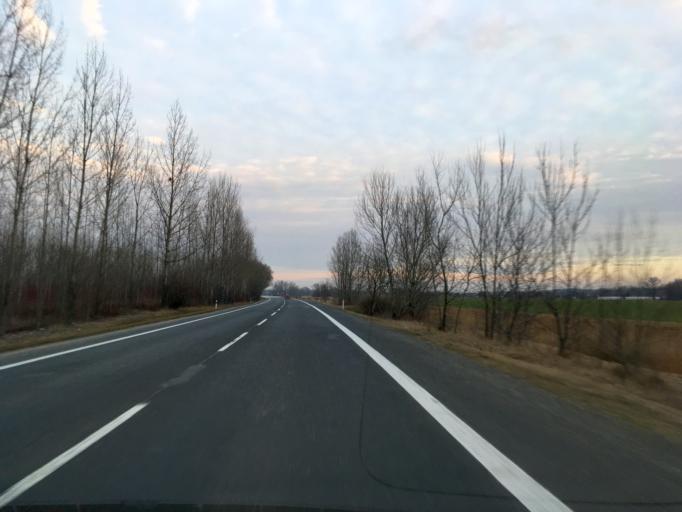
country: HU
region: Komarom-Esztergom
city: Acs
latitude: 47.7687
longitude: 17.9641
